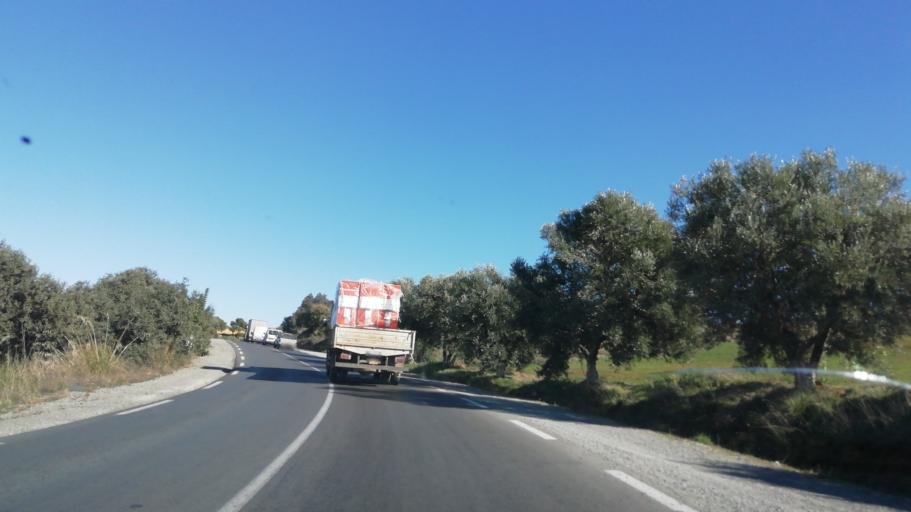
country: DZ
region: Mascara
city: Mascara
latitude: 35.5231
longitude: 0.3226
